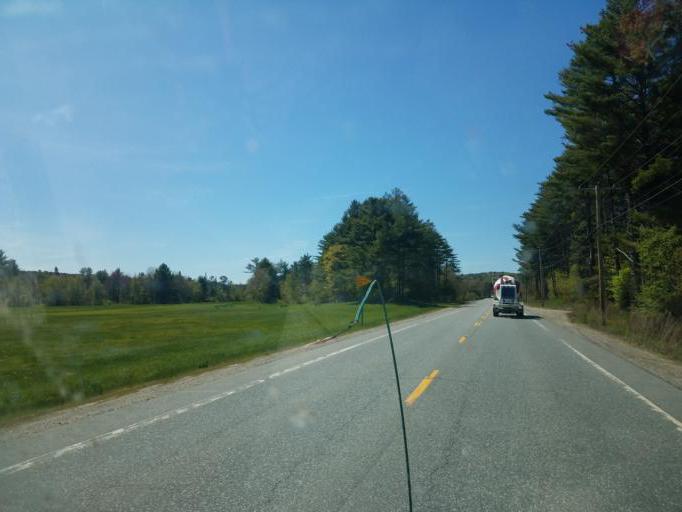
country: US
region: New Hampshire
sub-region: Grafton County
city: Enfield
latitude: 43.6488
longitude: -72.0559
